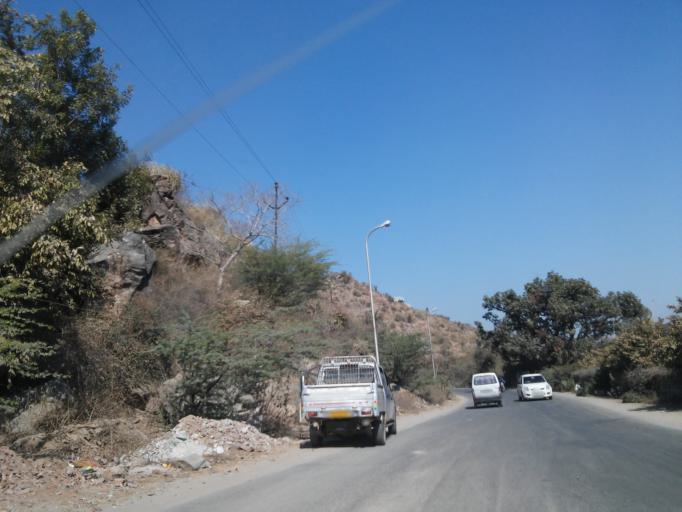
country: IN
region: Rajasthan
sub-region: Udaipur
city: Udaipur
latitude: 24.5723
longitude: 73.6539
